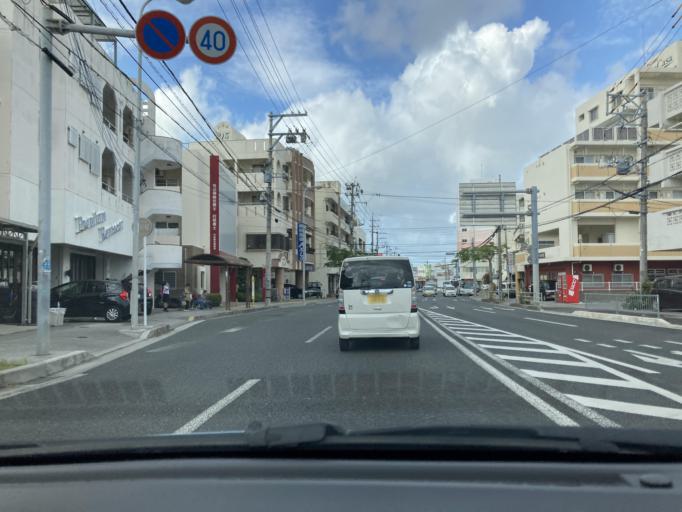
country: JP
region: Okinawa
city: Tomigusuku
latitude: 26.1945
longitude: 127.6761
